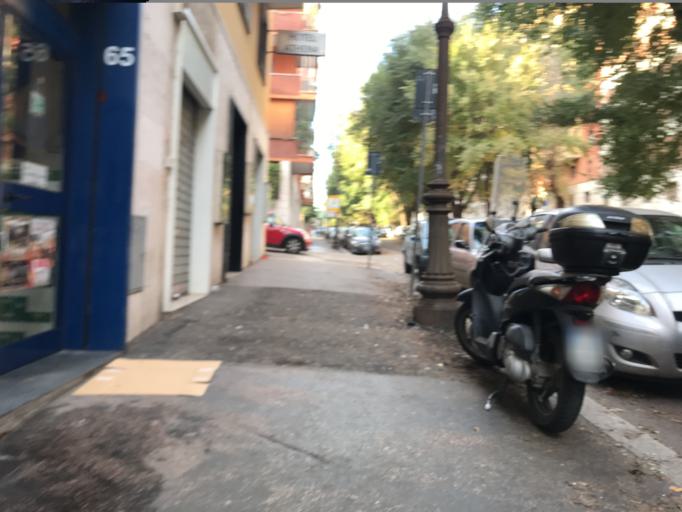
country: IT
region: Latium
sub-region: Citta metropolitana di Roma Capitale
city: Rome
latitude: 41.9086
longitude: 12.5193
